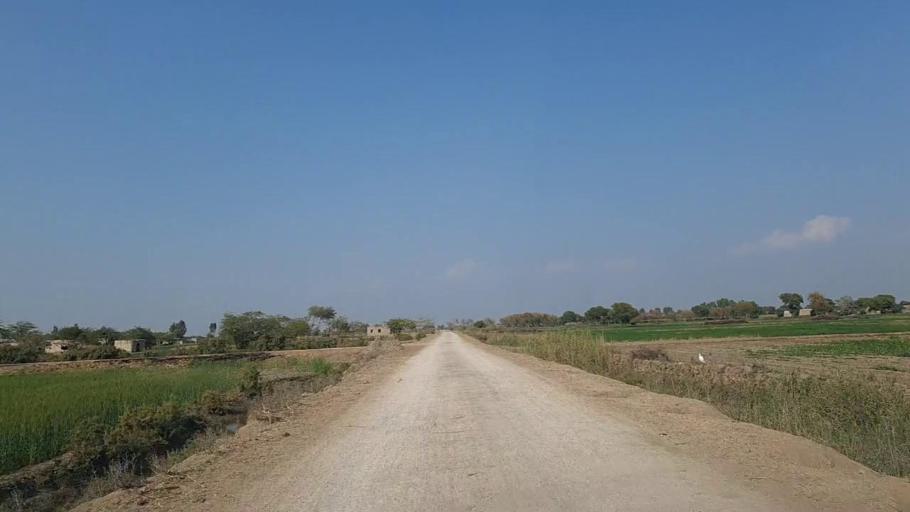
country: PK
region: Sindh
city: Jam Sahib
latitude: 26.2948
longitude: 68.5832
